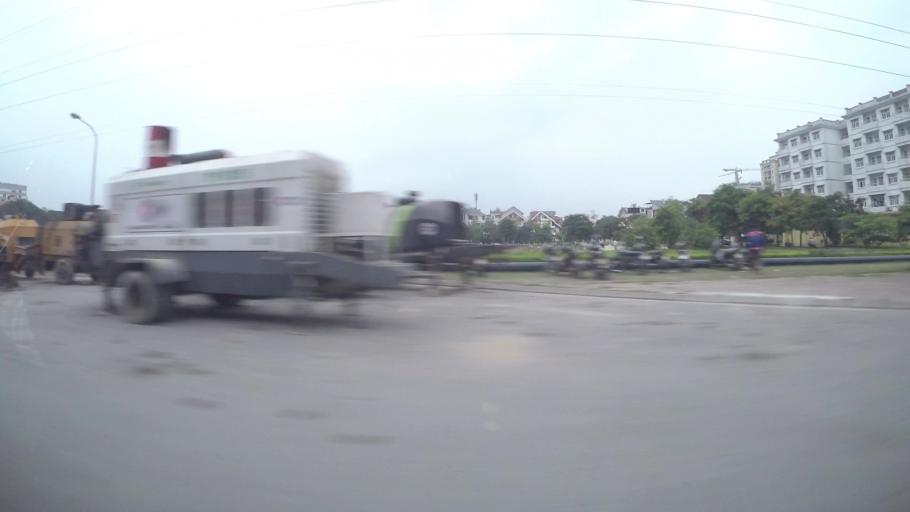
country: VN
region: Ha Noi
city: Trau Quy
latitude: 21.0370
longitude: 105.9068
